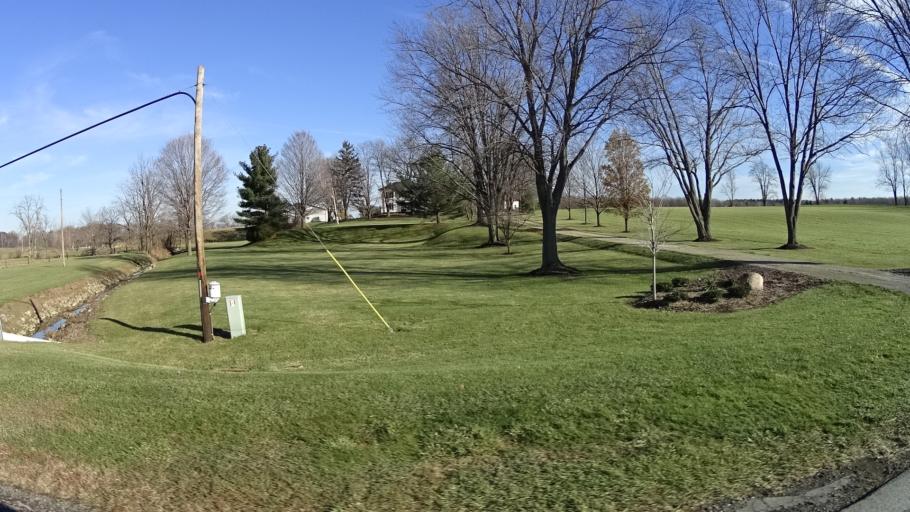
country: US
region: Ohio
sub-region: Lorain County
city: Wellington
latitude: 41.1451
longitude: -82.2181
